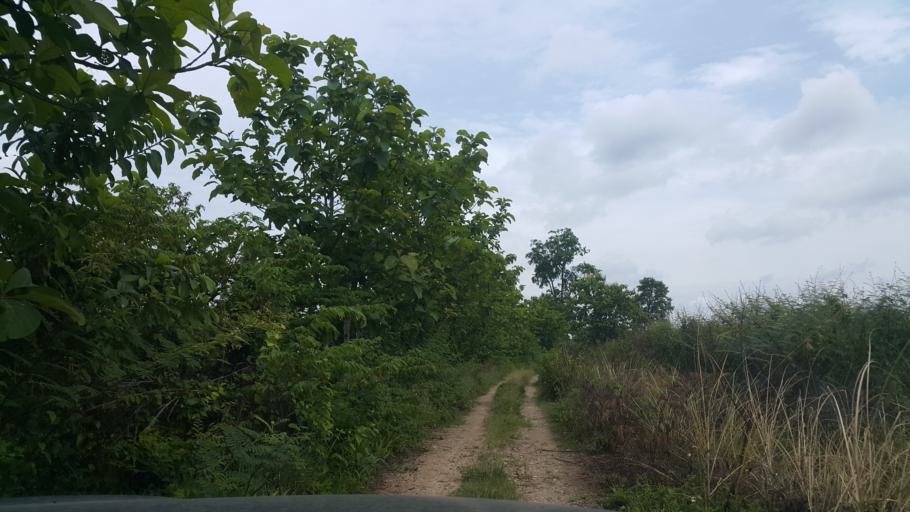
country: TH
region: Lamphun
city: Ban Thi
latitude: 18.6328
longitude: 99.1569
